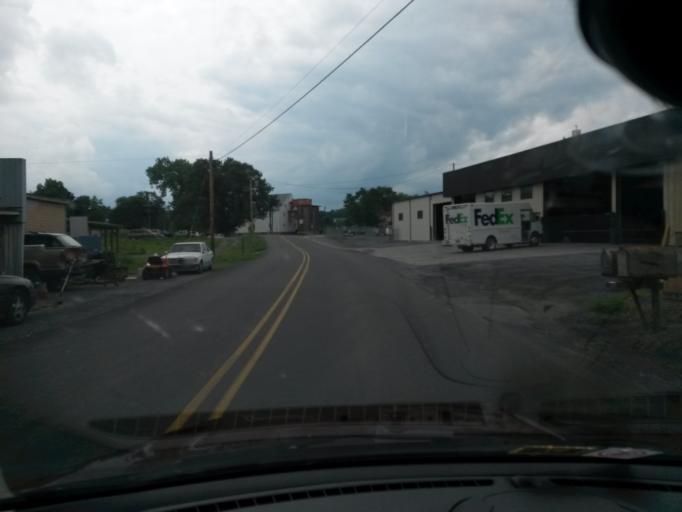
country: US
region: Virginia
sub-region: Rockingham County
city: Dayton
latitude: 38.4210
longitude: -78.9389
